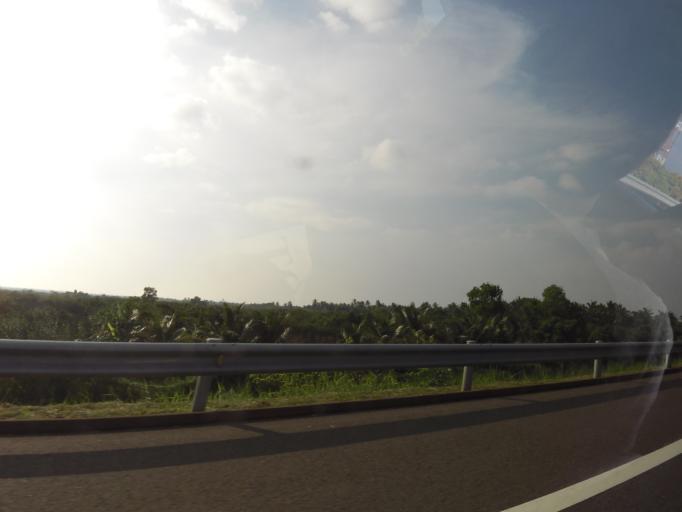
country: LK
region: Western
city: Ja Ela
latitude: 7.1048
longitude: 79.8777
